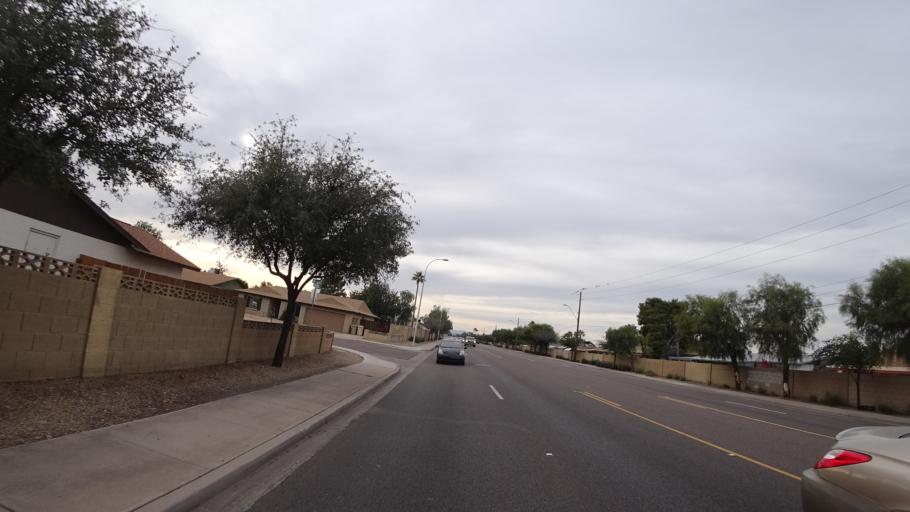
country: US
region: Arizona
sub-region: Maricopa County
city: Glendale
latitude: 33.5819
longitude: -112.1626
